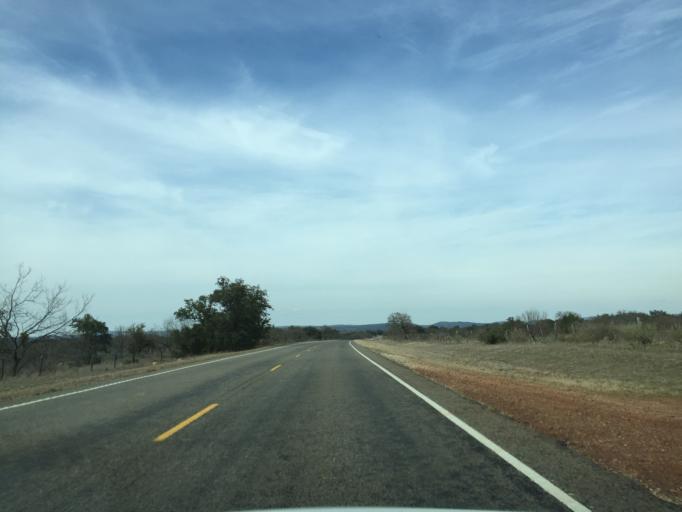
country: US
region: Texas
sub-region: Llano County
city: Llano
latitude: 30.5036
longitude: -98.7072
